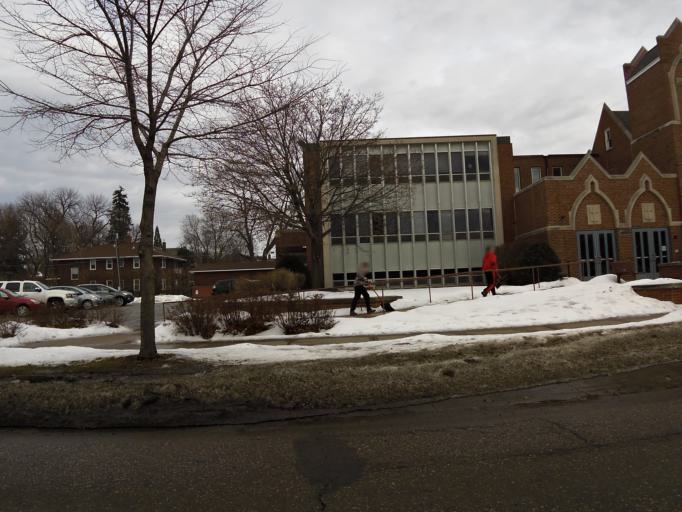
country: US
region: Minnesota
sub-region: Ramsey County
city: Falcon Heights
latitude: 44.9385
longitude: -93.1670
